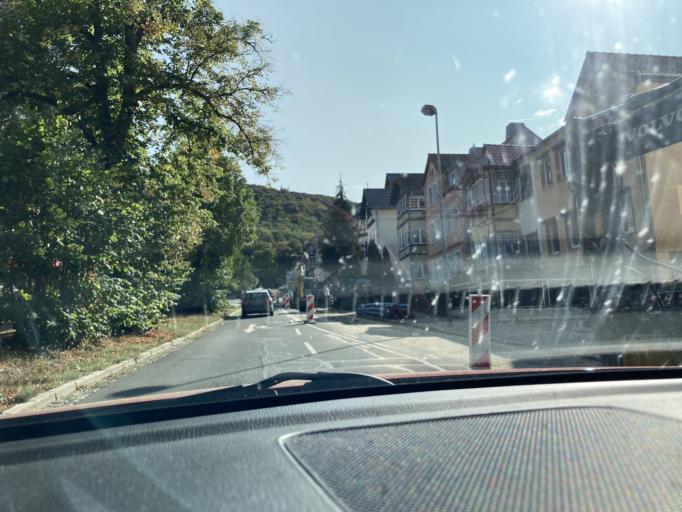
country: DE
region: Saxony-Anhalt
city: Thale
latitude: 51.7421
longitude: 11.0381
